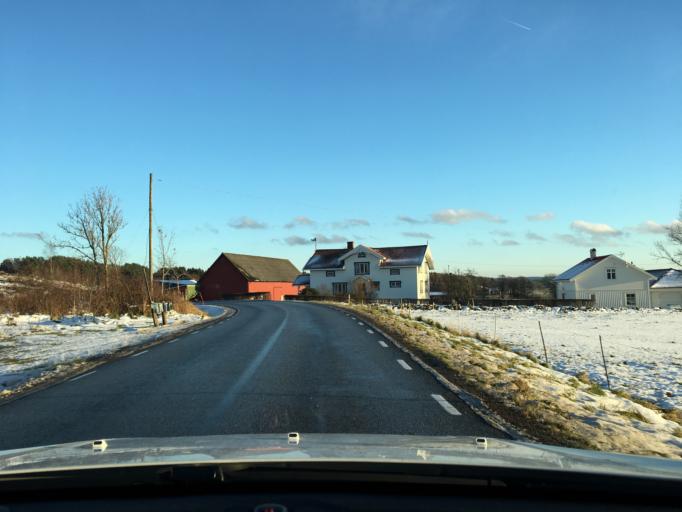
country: SE
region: Vaestra Goetaland
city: Svanesund
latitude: 58.1413
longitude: 11.7893
